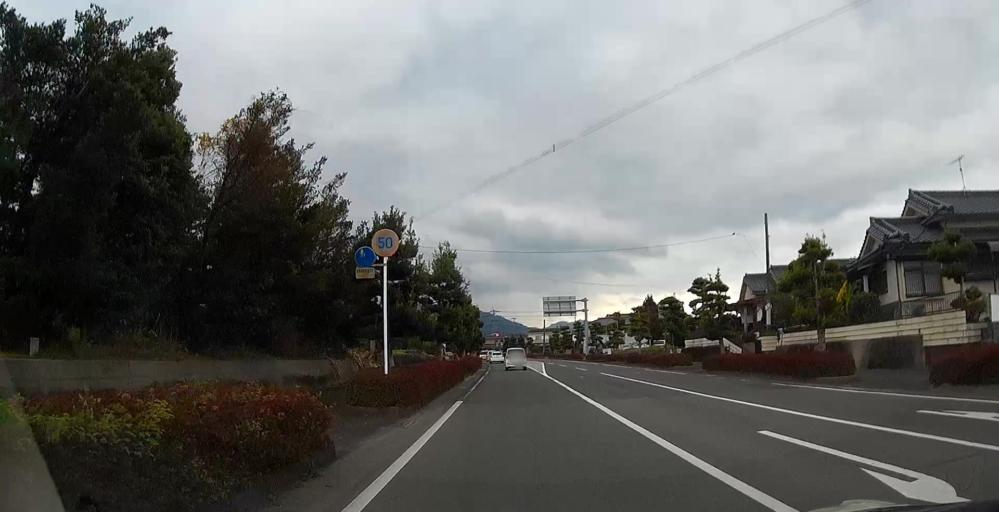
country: JP
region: Kagoshima
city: Izumi
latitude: 32.0822
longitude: 130.3444
